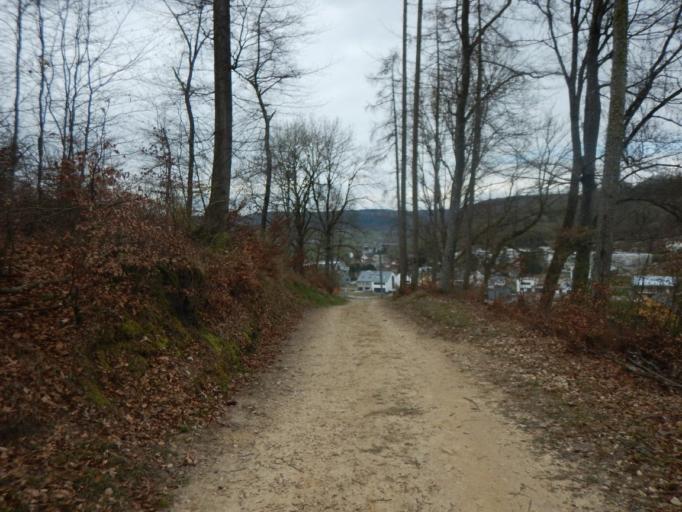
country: LU
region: Luxembourg
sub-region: Canton de Mersch
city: Lorentzweiler
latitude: 49.7002
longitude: 6.1529
